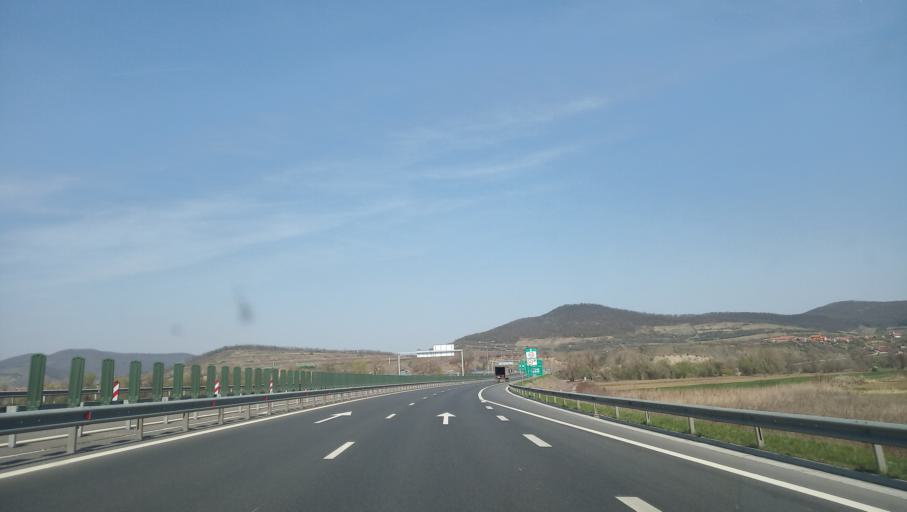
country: RO
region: Alba
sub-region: Municipiul Aiud
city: Aiud
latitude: 46.3327
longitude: 23.7298
